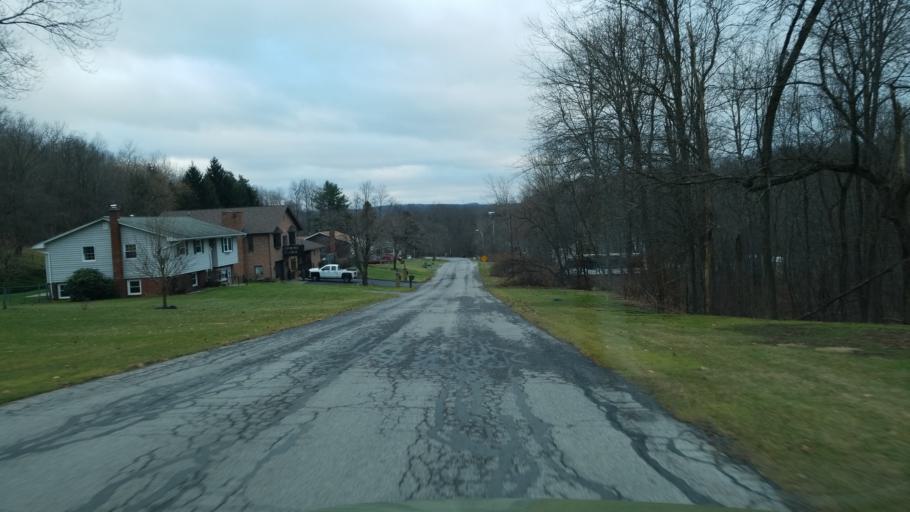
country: US
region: Pennsylvania
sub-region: Jefferson County
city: Falls Creek
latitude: 41.1406
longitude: -78.8106
